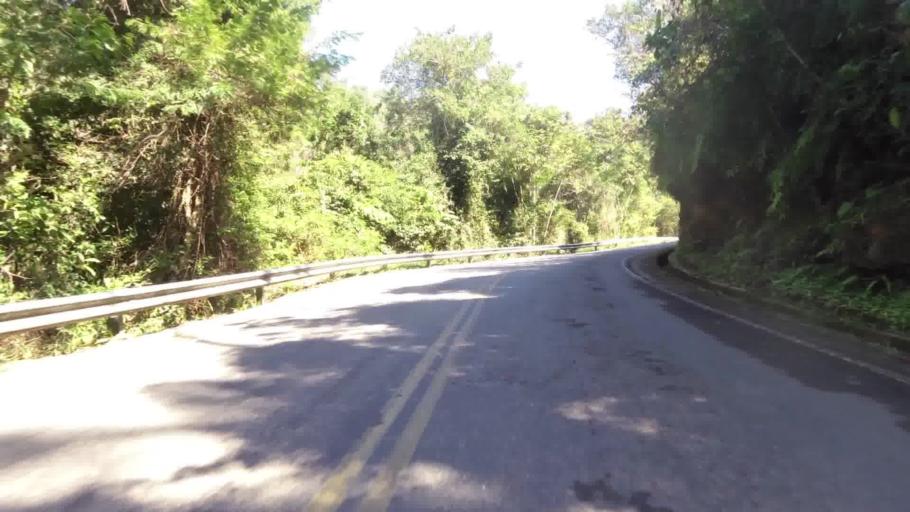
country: BR
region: Espirito Santo
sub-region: Alfredo Chaves
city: Alfredo Chaves
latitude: -20.5747
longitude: -40.8058
